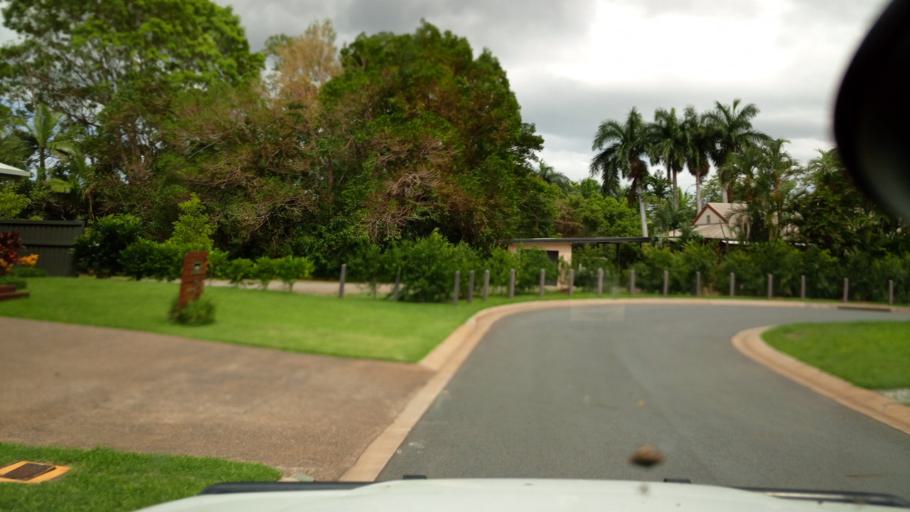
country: AU
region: Queensland
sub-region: Cairns
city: Redlynch
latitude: -16.8971
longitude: 145.6939
